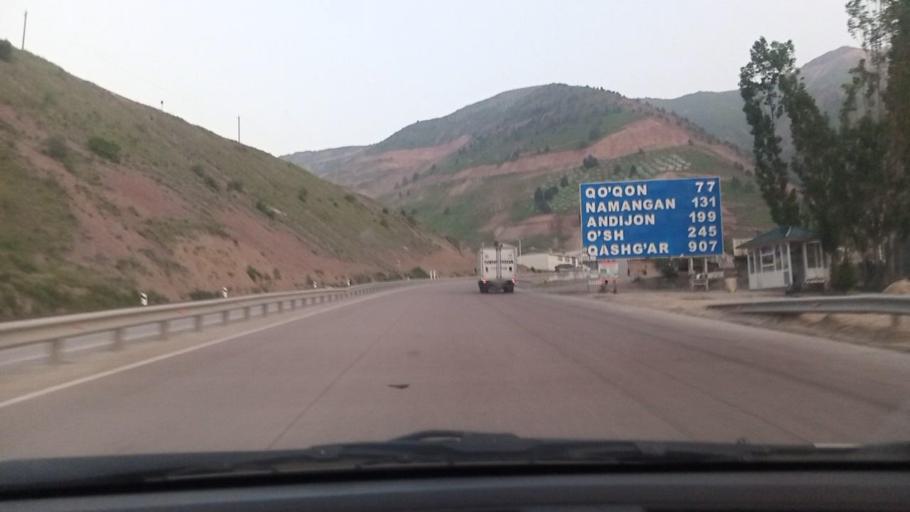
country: UZ
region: Toshkent
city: Angren
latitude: 41.1114
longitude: 70.4981
